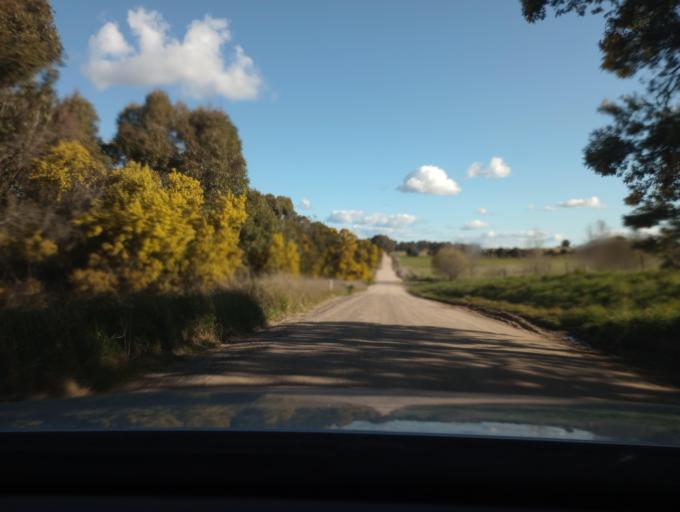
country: AU
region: New South Wales
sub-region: Blayney
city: Millthorpe
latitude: -33.4040
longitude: 149.3077
